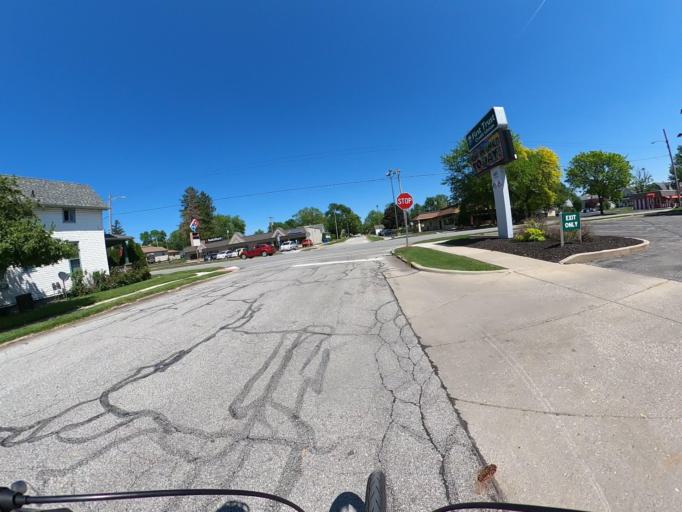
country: US
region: Indiana
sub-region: LaPorte County
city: LaPorte
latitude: 41.6039
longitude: -86.7305
